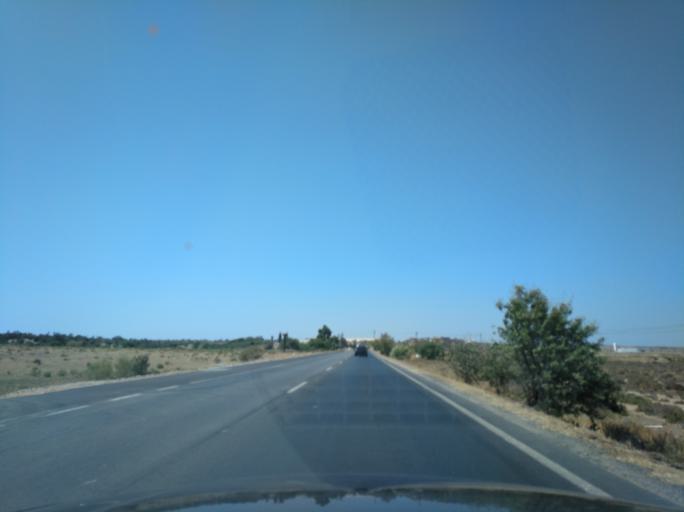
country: PT
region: Faro
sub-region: Castro Marim
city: Castro Marim
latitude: 37.2054
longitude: -7.4334
